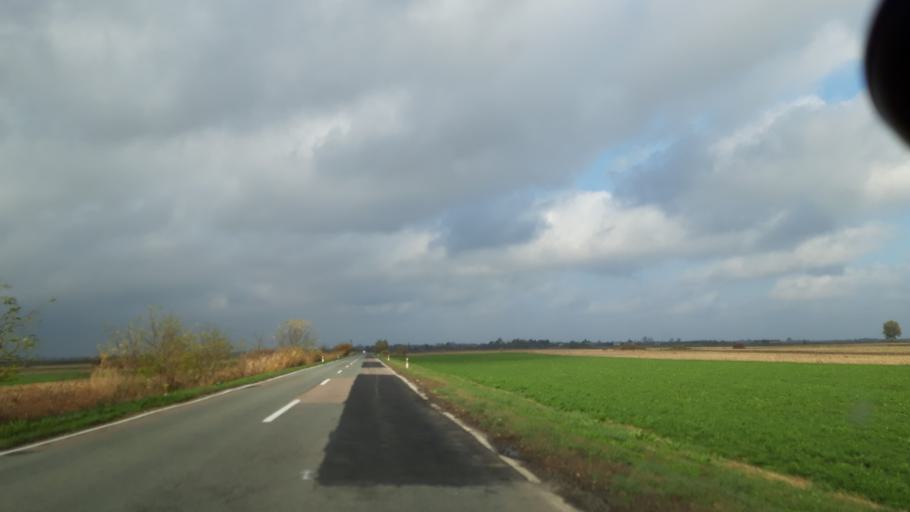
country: RS
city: Ostojicevo
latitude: 45.9125
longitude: 20.1516
